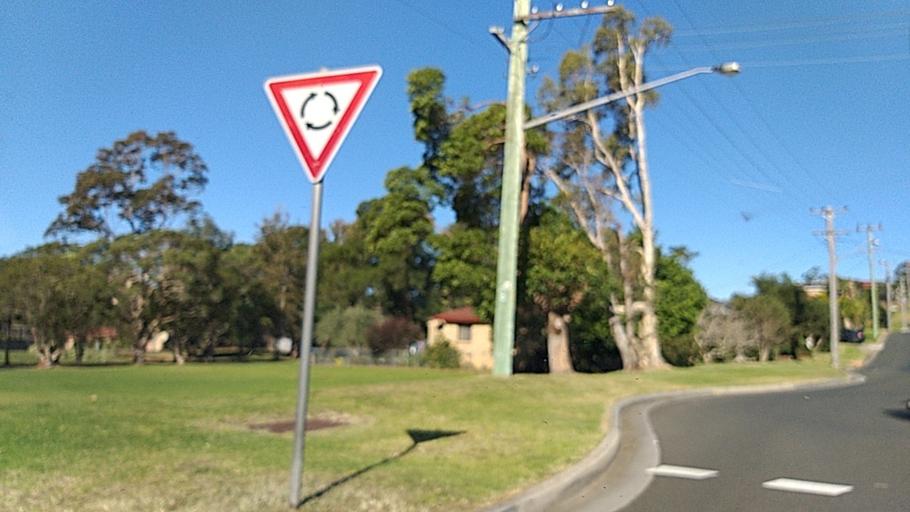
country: AU
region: New South Wales
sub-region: Wollongong
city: Mount Keira
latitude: -34.4185
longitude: 150.8555
